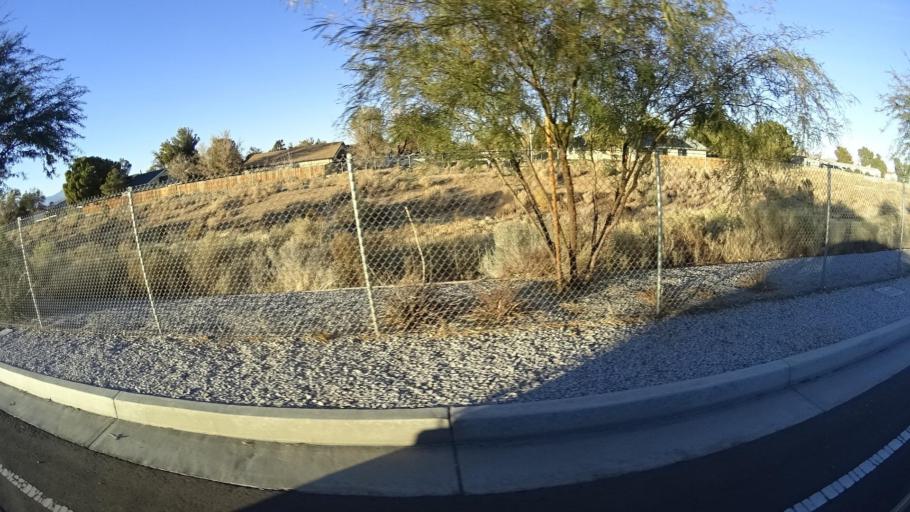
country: US
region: California
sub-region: Kern County
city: Ridgecrest
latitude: 35.6080
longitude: -117.6663
